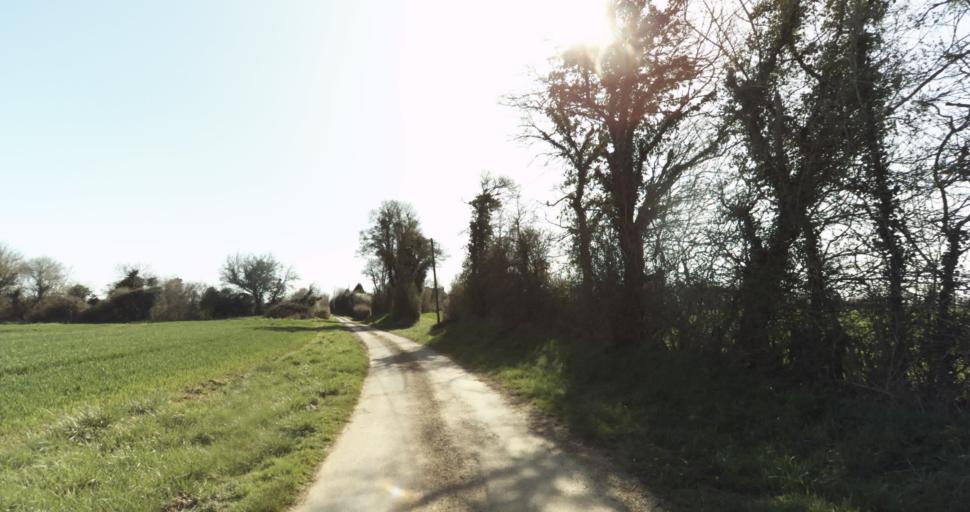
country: FR
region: Lower Normandy
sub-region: Departement de l'Orne
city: Trun
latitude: 48.9281
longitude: -0.0000
